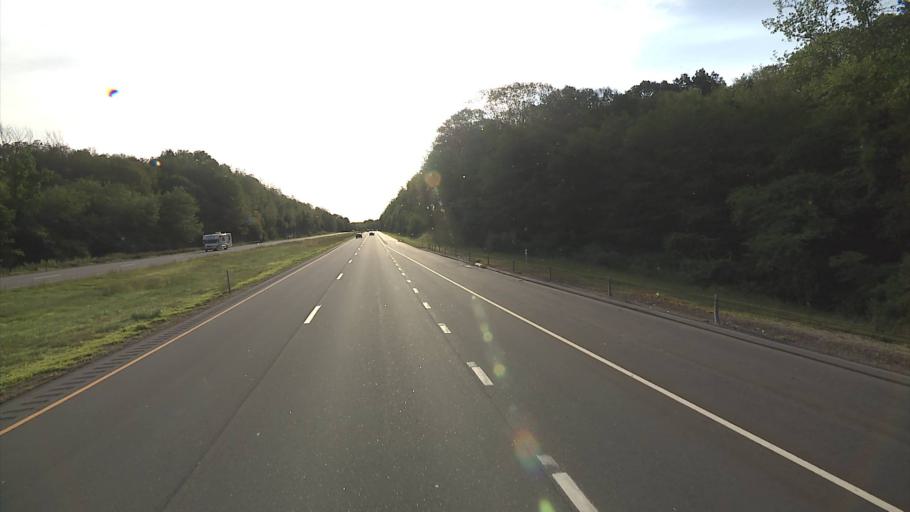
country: US
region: Connecticut
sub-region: New London County
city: Montville Center
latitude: 41.5709
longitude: -72.2015
